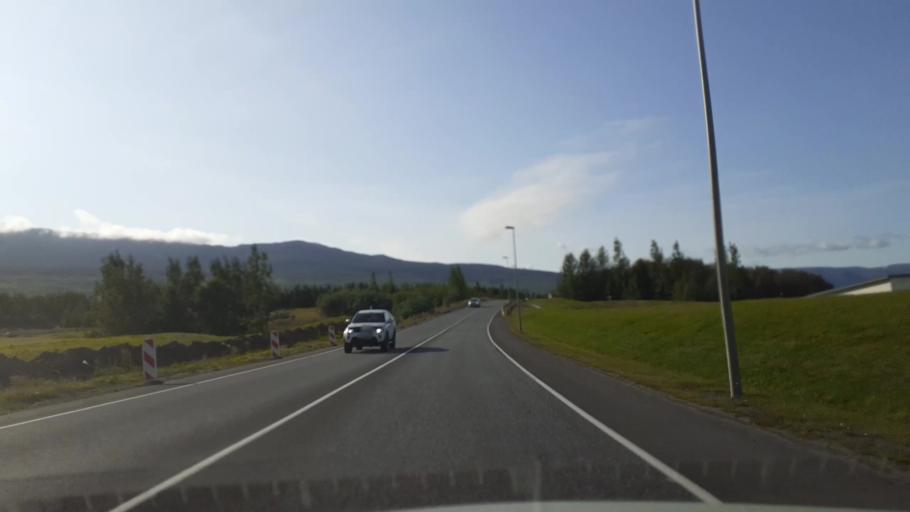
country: IS
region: Northeast
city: Akureyri
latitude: 65.6722
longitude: -18.1208
